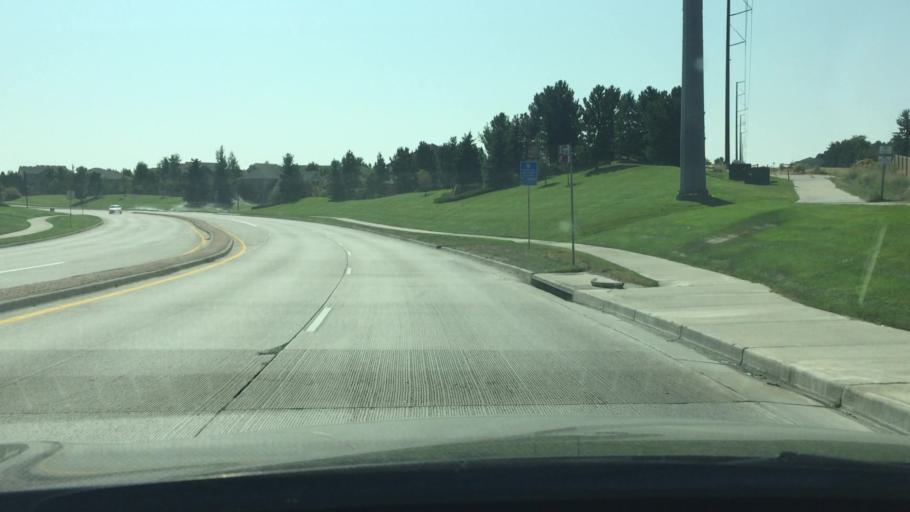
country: US
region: Colorado
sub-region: Arapahoe County
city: Dove Valley
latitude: 39.6085
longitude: -104.7916
